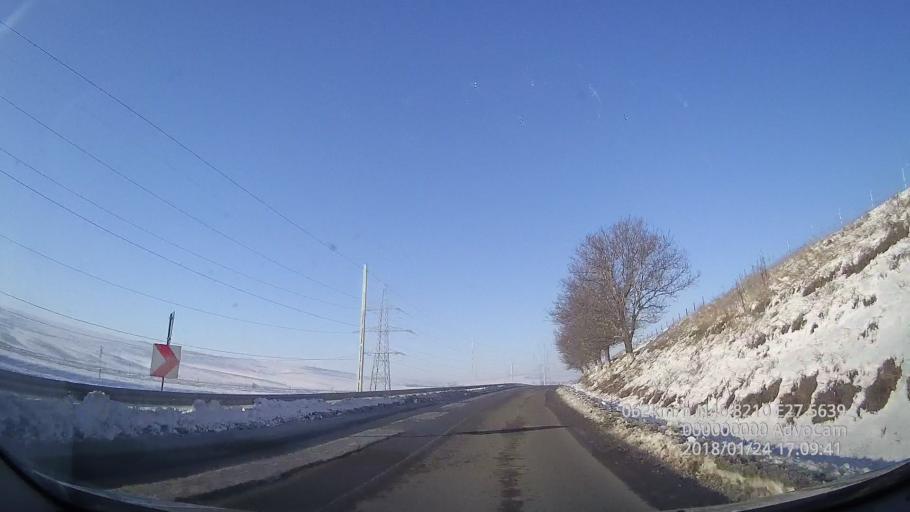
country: RO
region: Vaslui
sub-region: Comuna Vulturesti
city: Vulturesti
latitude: 46.8215
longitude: 27.5637
